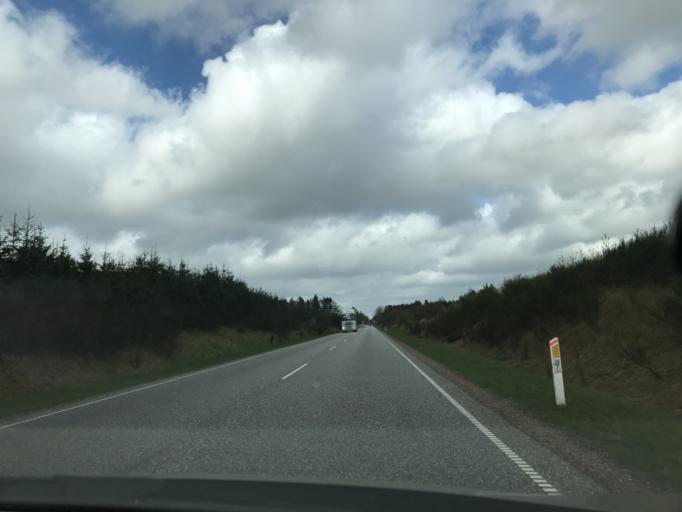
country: DK
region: Central Jutland
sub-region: Herning Kommune
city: Sunds
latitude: 56.3780
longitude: 8.9869
